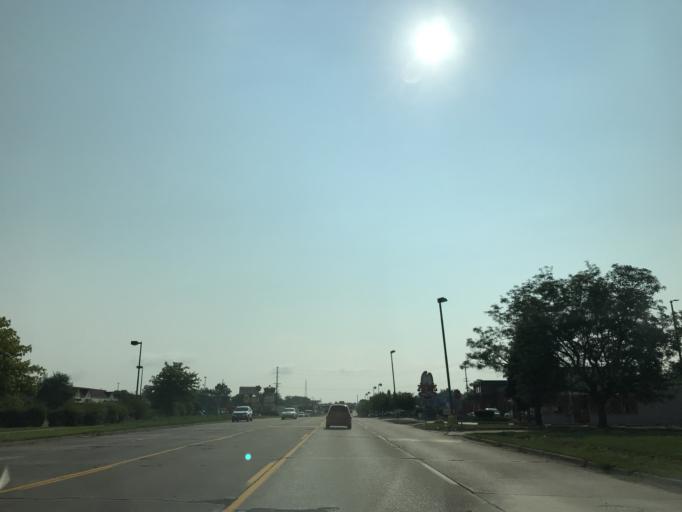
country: US
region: Michigan
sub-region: Washtenaw County
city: Ypsilanti
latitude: 42.2499
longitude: -83.6590
